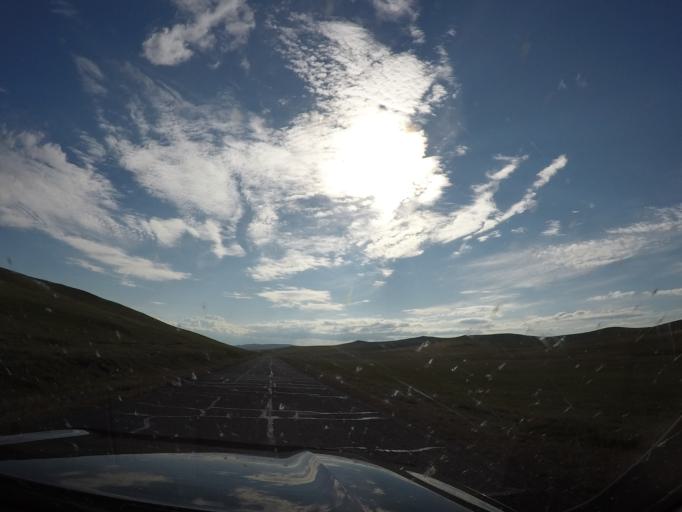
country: MN
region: Hentiy
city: Modot
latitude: 47.7891
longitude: 108.6757
